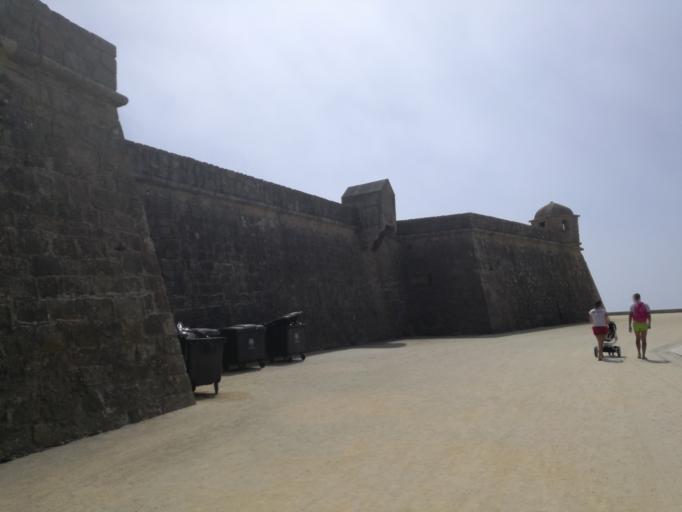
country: PT
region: Porto
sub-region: Vila do Conde
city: Vila do Conde
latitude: 41.3421
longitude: -8.7518
